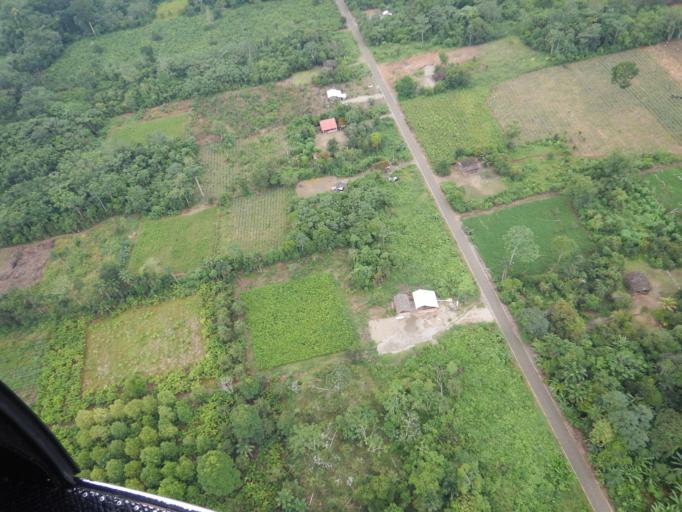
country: BO
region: Cochabamba
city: Chimore
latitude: -17.2336
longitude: -64.6890
